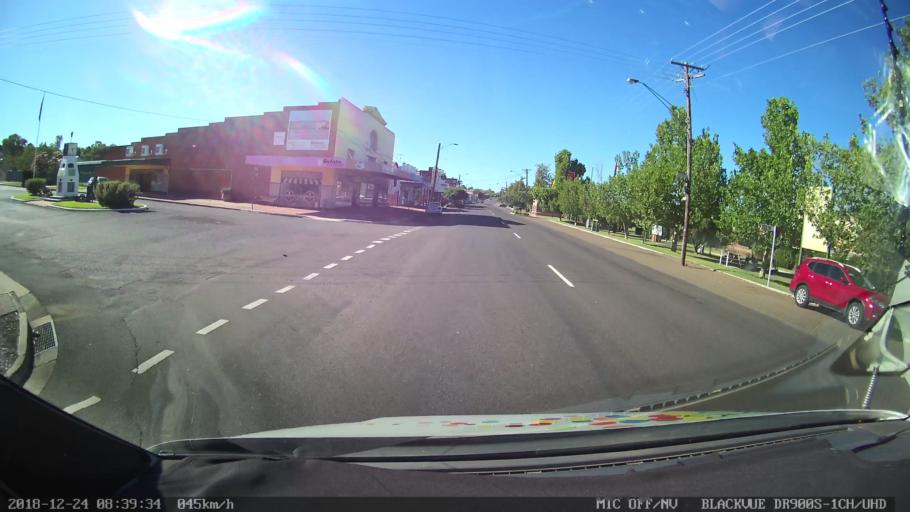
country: AU
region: New South Wales
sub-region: Liverpool Plains
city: Quirindi
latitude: -31.3489
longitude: 150.6472
